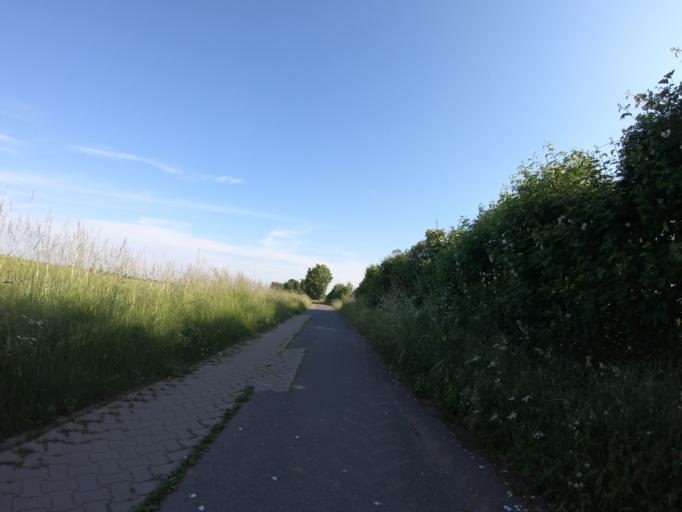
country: DE
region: Lower Saxony
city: Meine
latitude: 52.3708
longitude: 10.5441
